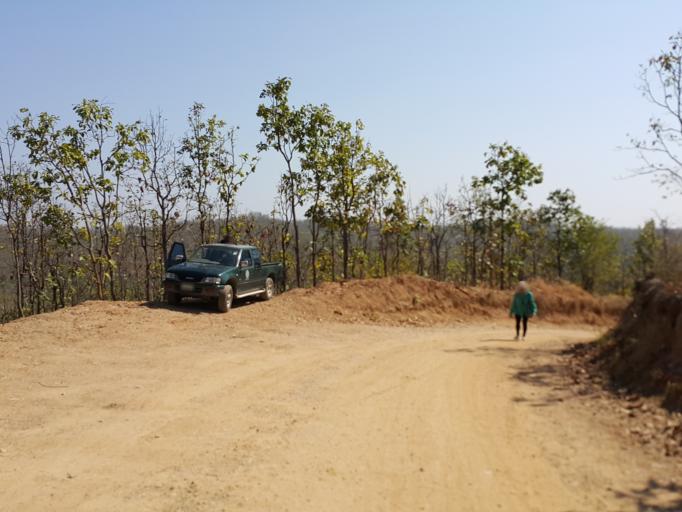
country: TH
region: Chiang Mai
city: Doi Lo
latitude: 18.5186
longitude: 98.7406
